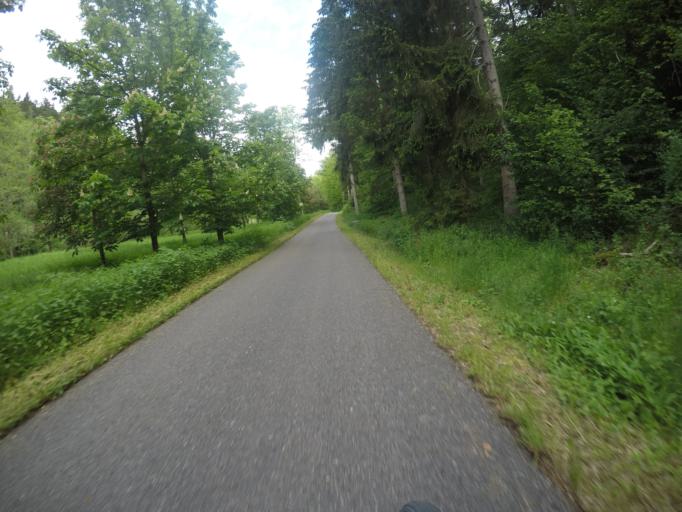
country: DE
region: Baden-Wuerttemberg
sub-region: Karlsruhe Region
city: Wildberg
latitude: 48.6064
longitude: 8.7363
